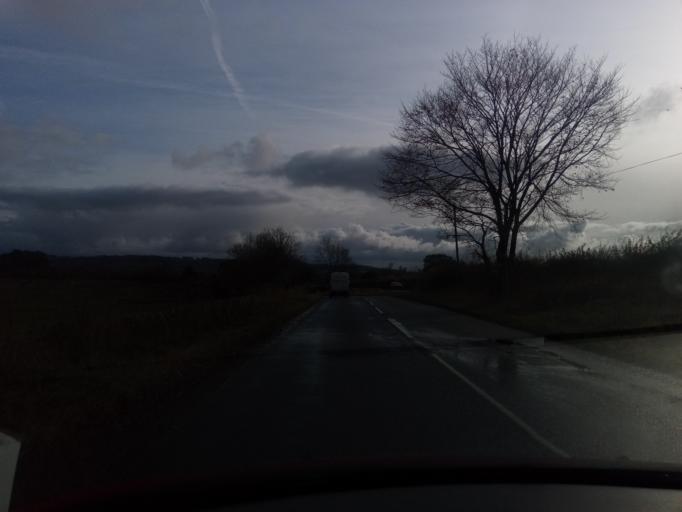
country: GB
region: England
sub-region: Northumberland
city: Wall
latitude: 55.0445
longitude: -2.1514
